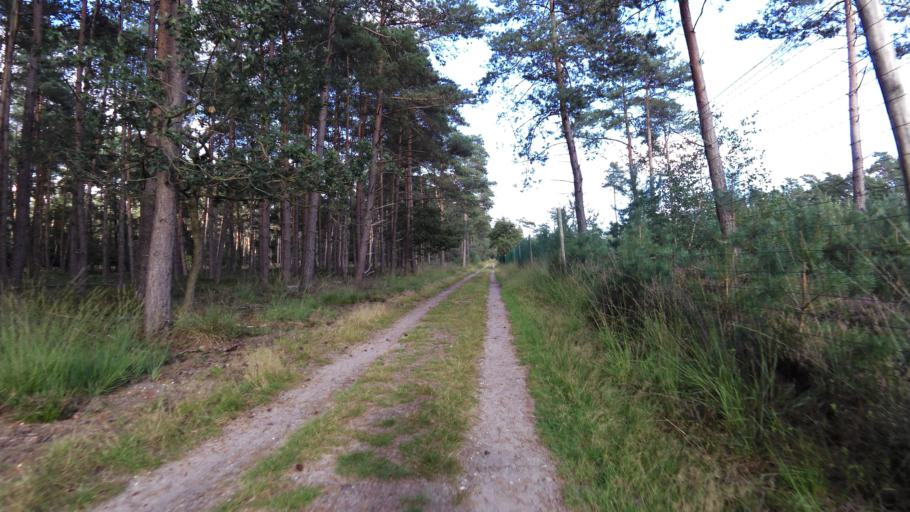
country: NL
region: Gelderland
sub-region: Gemeente Apeldoorn
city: Uddel
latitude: 52.2574
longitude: 5.8055
